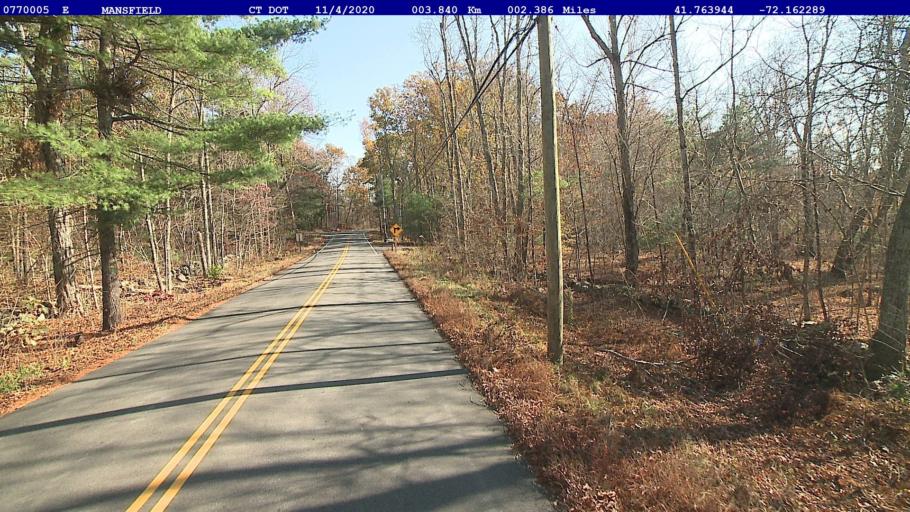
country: US
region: Connecticut
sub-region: Windham County
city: Windham
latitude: 41.7640
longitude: -72.1623
